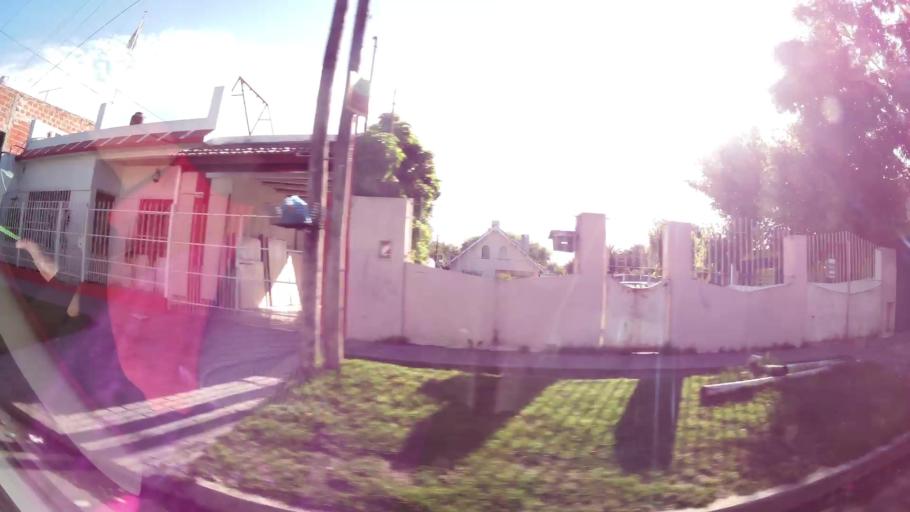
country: AR
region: Buenos Aires
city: Santa Catalina - Dique Lujan
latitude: -34.4908
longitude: -58.7099
